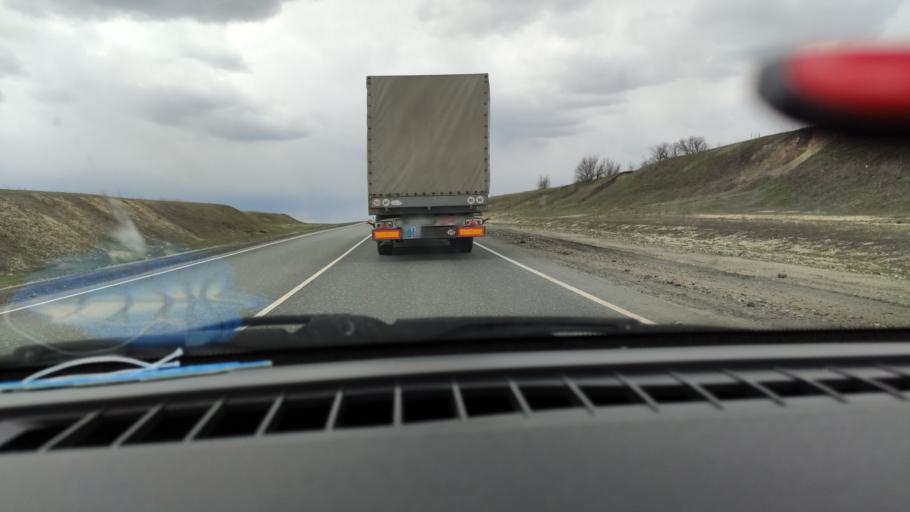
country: RU
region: Saratov
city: Sennoy
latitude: 52.1354
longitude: 46.8711
